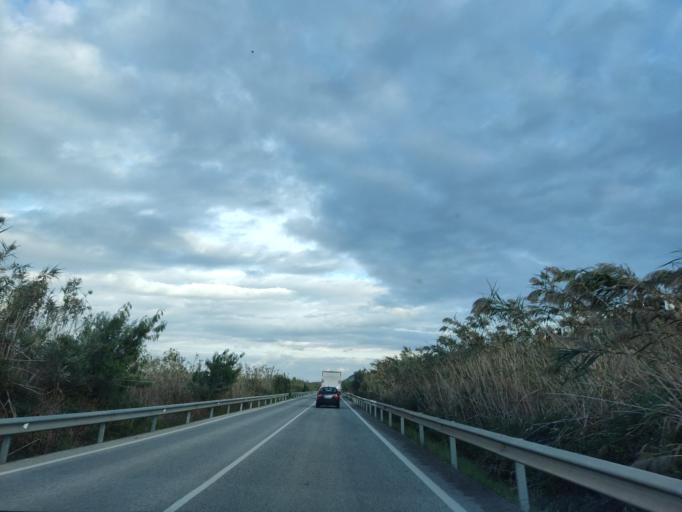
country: ES
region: Valencia
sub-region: Provincia de Alicante
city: Benimeli
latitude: 38.8529
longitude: -0.0494
